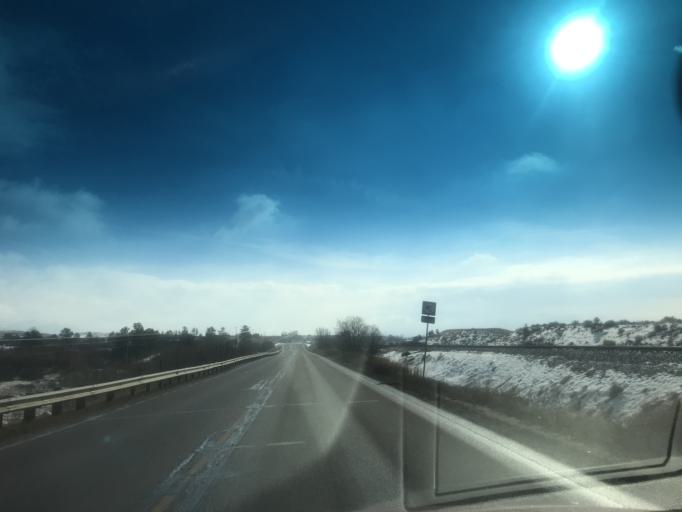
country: US
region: Colorado
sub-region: Douglas County
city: Castle Pines
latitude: 39.4557
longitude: -104.9812
